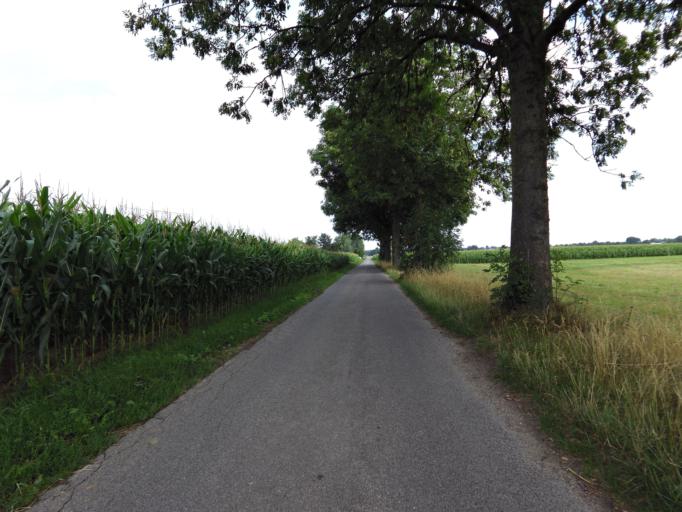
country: DE
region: North Rhine-Westphalia
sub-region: Regierungsbezirk Koln
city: Gangelt
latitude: 51.0048
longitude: 6.0430
